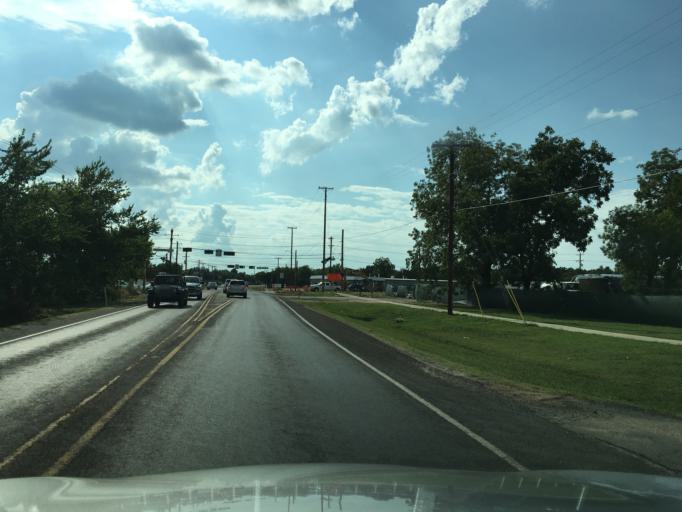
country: US
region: Texas
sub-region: Denton County
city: Denton
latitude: 33.2101
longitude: -97.0824
